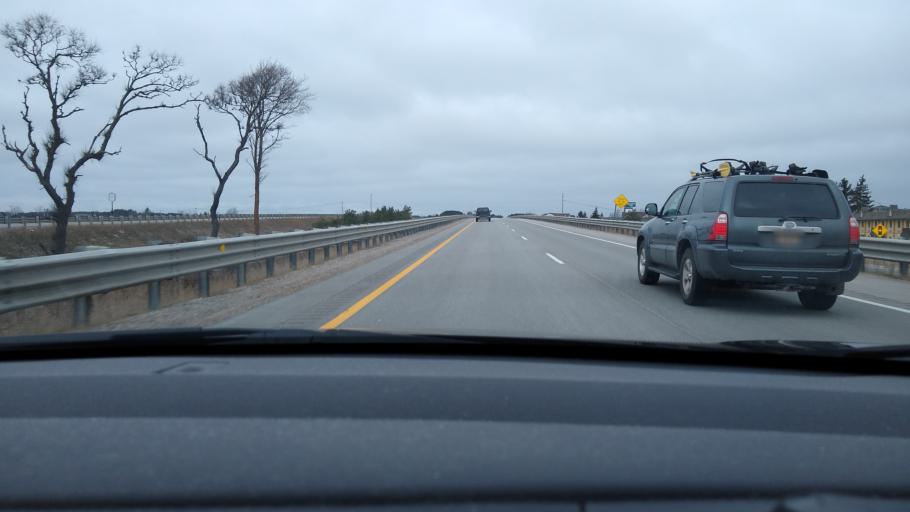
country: US
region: Michigan
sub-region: Otsego County
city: Gaylord
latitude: 45.0246
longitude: -84.6867
